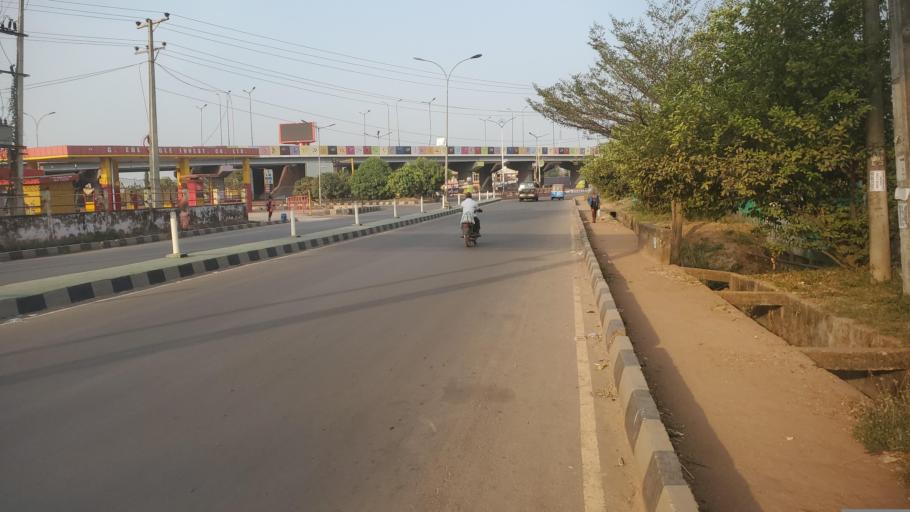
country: NG
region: Ebonyi
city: Abakaliki
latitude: 6.3258
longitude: 8.0851
